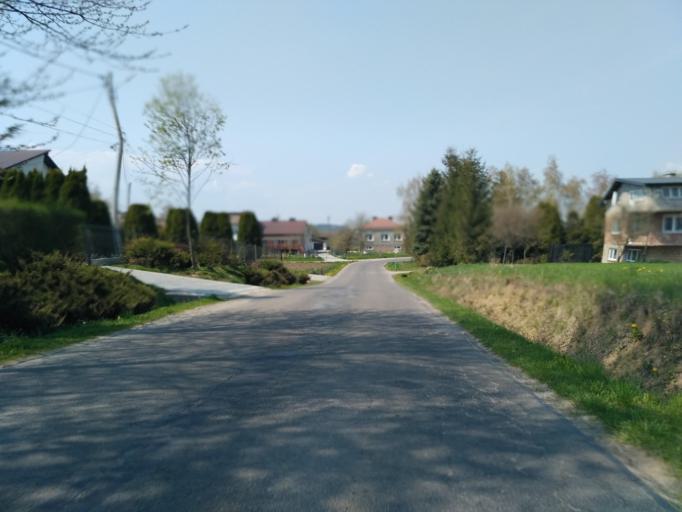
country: PL
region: Subcarpathian Voivodeship
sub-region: Powiat krosnienski
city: Chorkowka
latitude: 49.6620
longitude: 21.6375
